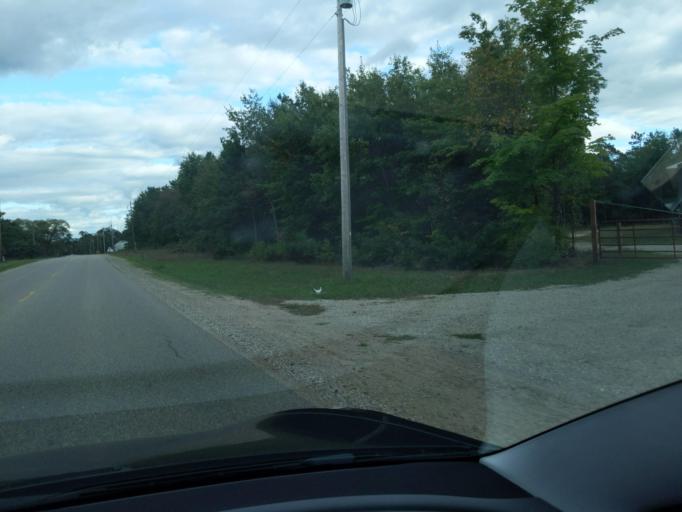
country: US
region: Michigan
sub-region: Kalkaska County
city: Rapid City
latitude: 44.8365
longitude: -85.2898
